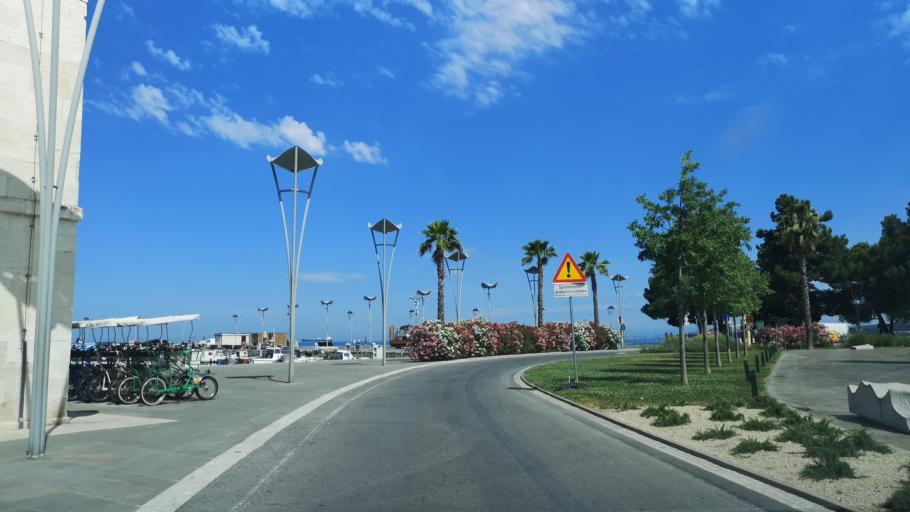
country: SI
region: Koper-Capodistria
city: Koper
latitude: 45.5483
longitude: 13.7250
